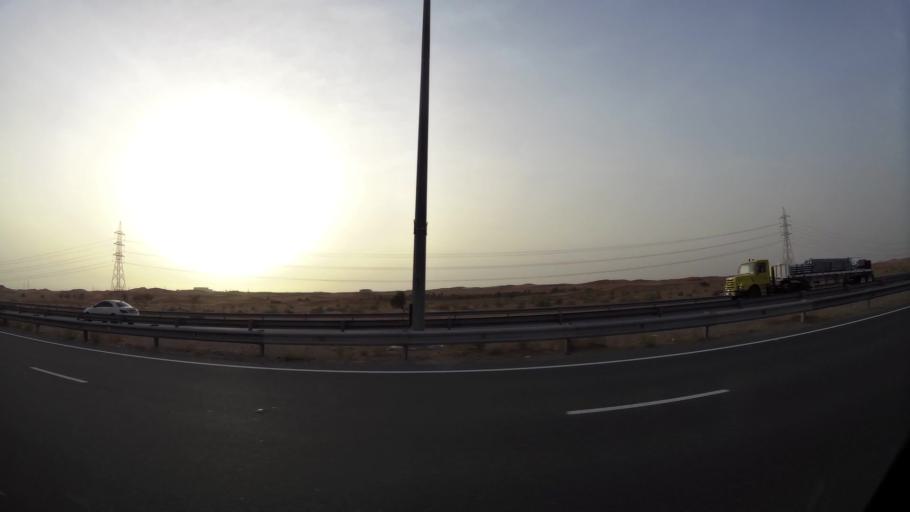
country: OM
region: Al Buraimi
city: Al Buraymi
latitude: 24.3360
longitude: 55.7691
